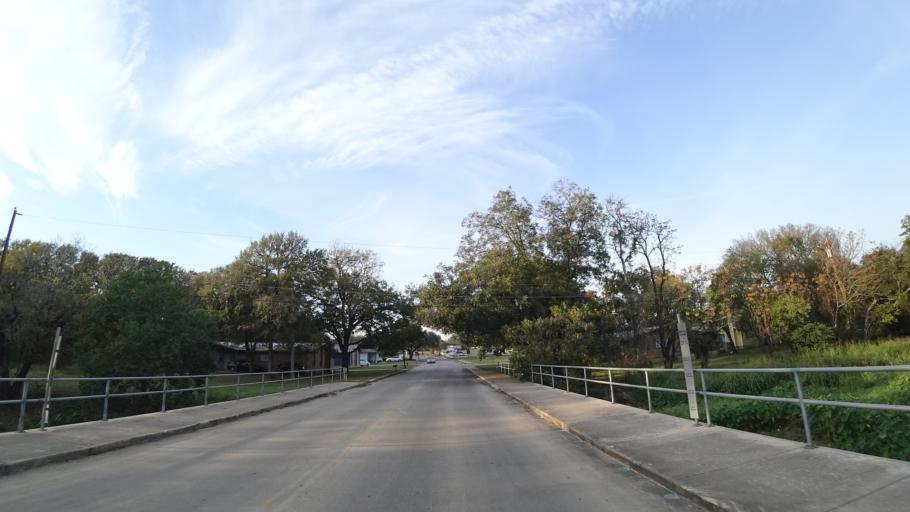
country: US
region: Texas
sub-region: Williamson County
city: Round Rock
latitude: 30.5063
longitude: -97.6741
